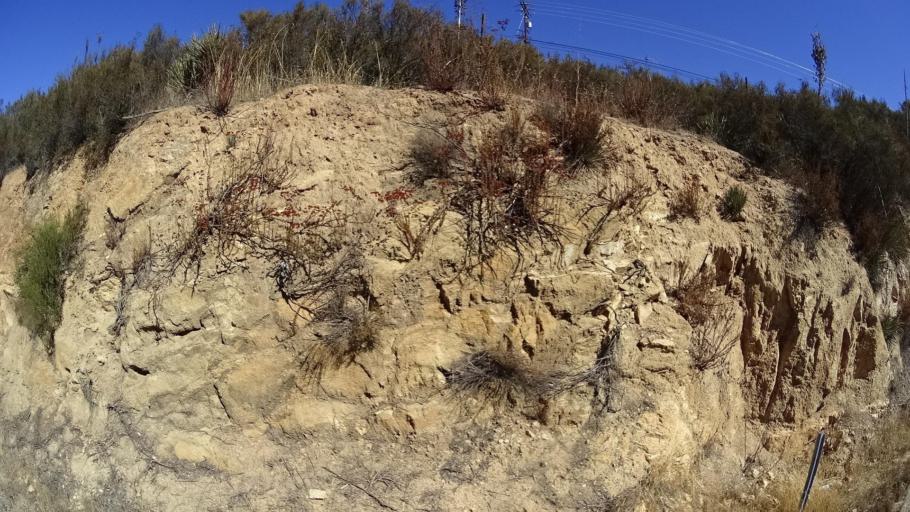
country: US
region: California
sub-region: San Diego County
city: Alpine
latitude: 32.7071
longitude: -116.7359
